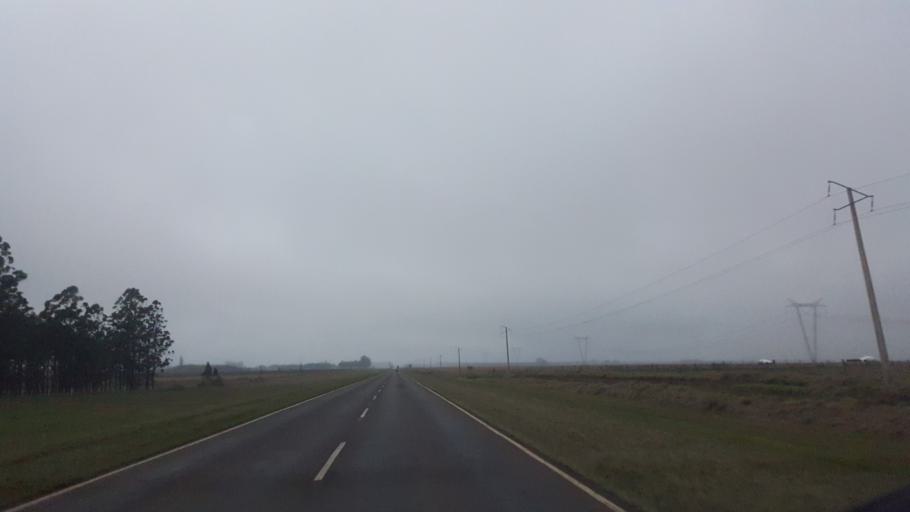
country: AR
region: Corrientes
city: Ituzaingo
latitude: -27.5908
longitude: -56.4789
